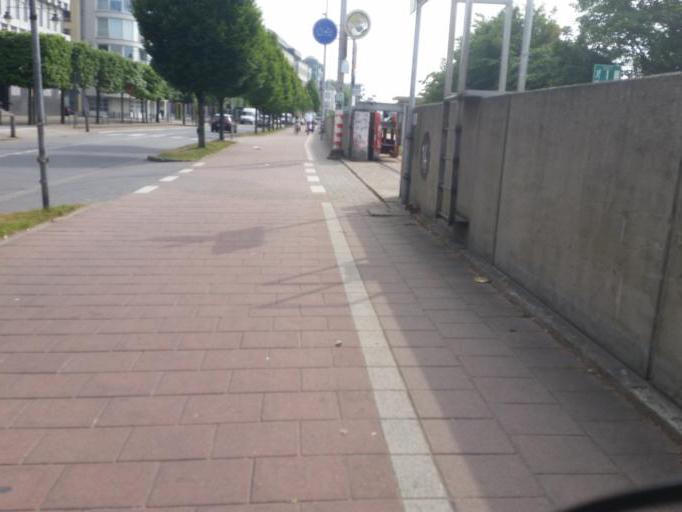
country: BE
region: Flanders
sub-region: Provincie Antwerpen
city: Antwerpen
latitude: 51.2108
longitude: 4.3883
